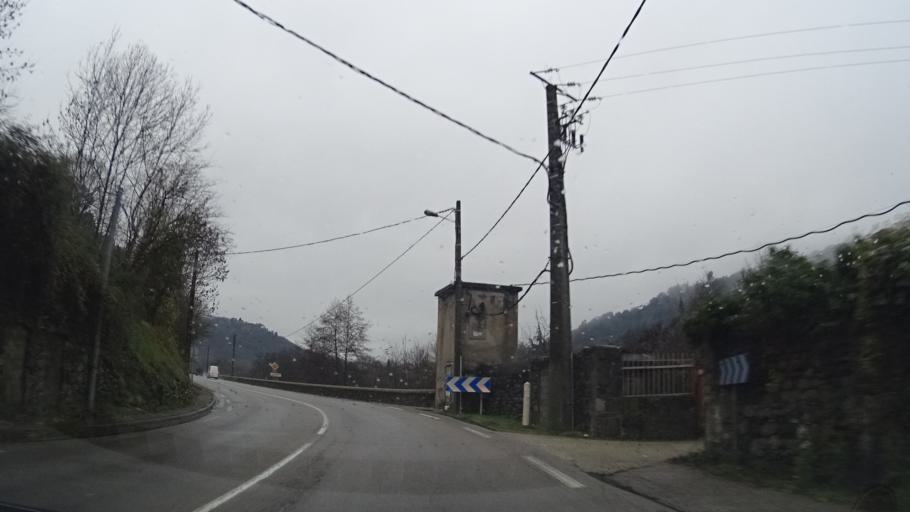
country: FR
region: Rhone-Alpes
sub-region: Departement de l'Ardeche
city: Labegude
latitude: 44.6449
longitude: 4.3489
